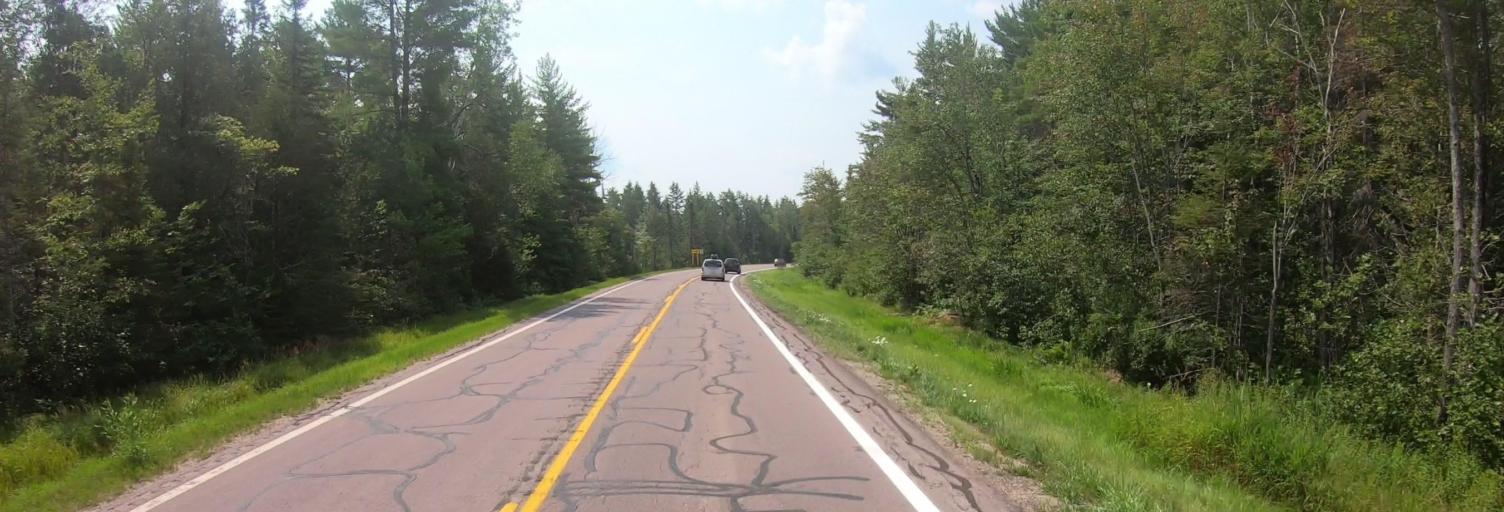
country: US
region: Michigan
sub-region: Luce County
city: Newberry
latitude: 46.4743
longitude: -85.4270
